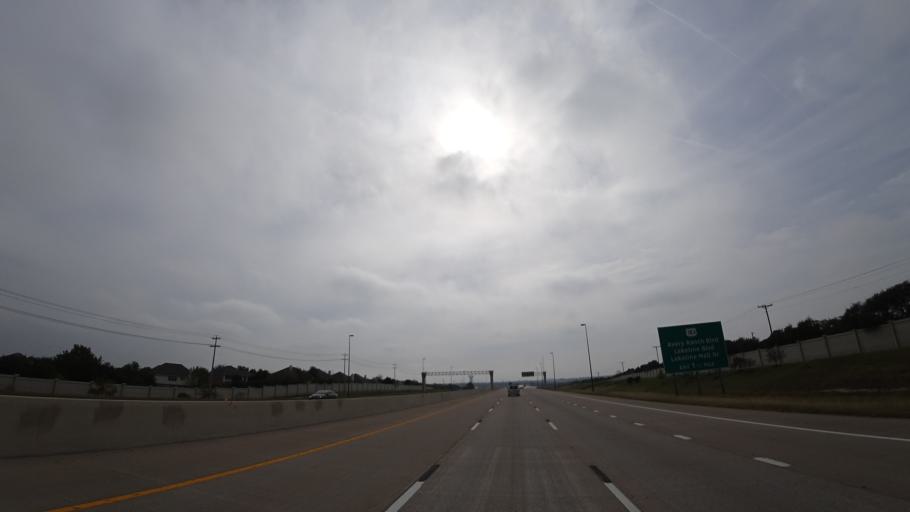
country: US
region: Texas
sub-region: Williamson County
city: Cedar Park
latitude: 30.5094
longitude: -97.8113
